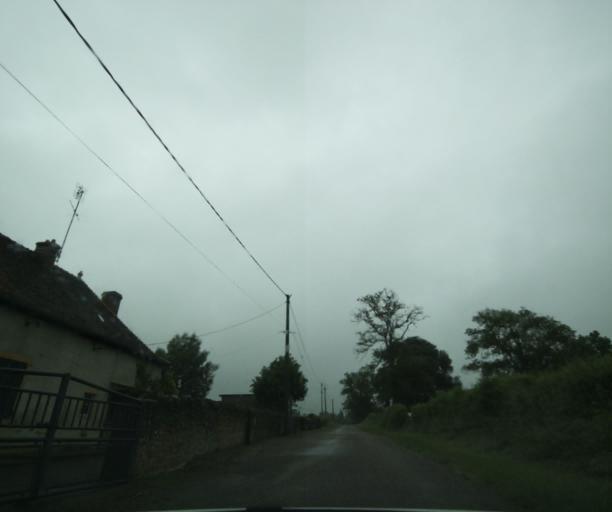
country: FR
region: Bourgogne
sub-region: Departement de Saone-et-Loire
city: Charolles
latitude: 46.4105
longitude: 4.2036
